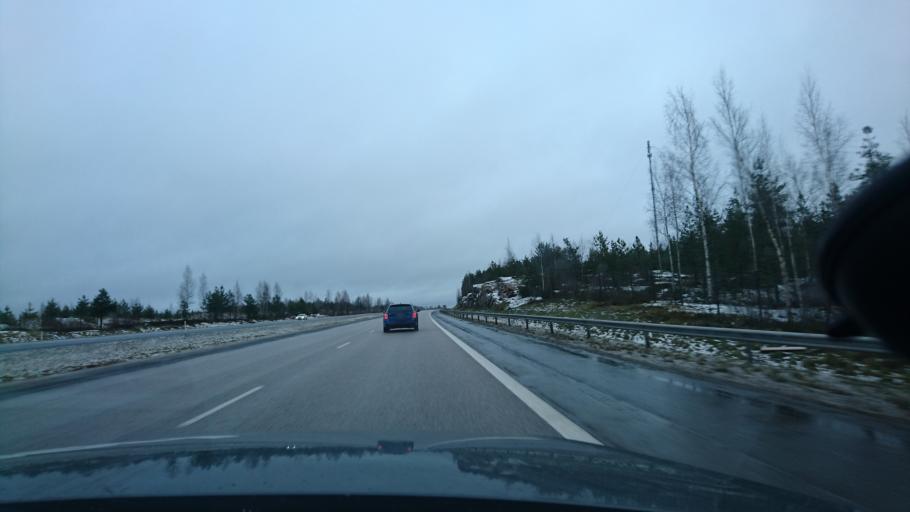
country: FI
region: Uusimaa
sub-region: Helsinki
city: Jaervenpaeae
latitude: 60.5644
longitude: 25.1936
